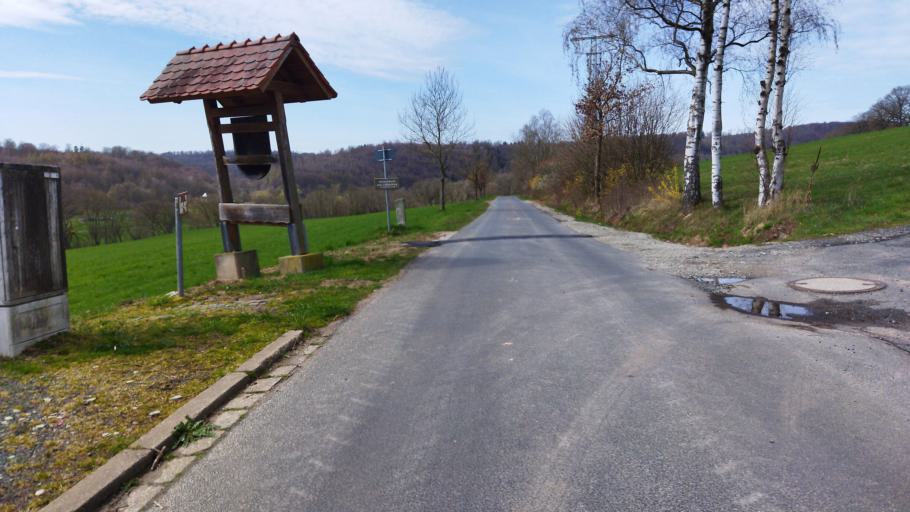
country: DE
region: Lower Saxony
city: Bodenfelde
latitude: 51.6301
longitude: 9.5127
